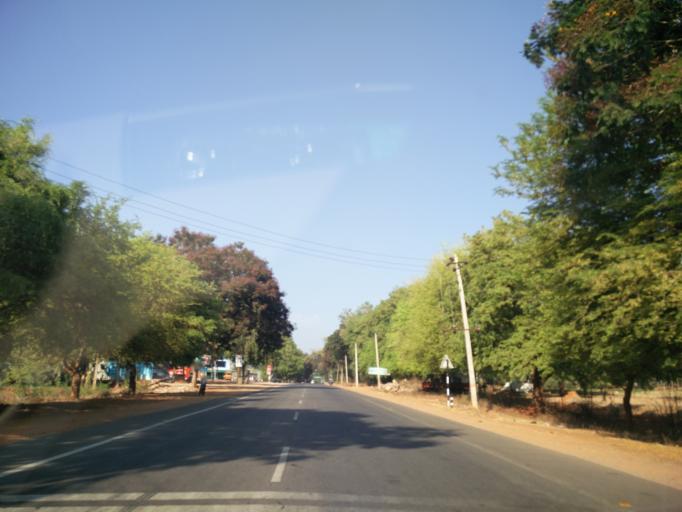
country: IN
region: Karnataka
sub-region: Tumkur
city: Gubbi
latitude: 13.3163
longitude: 76.9603
